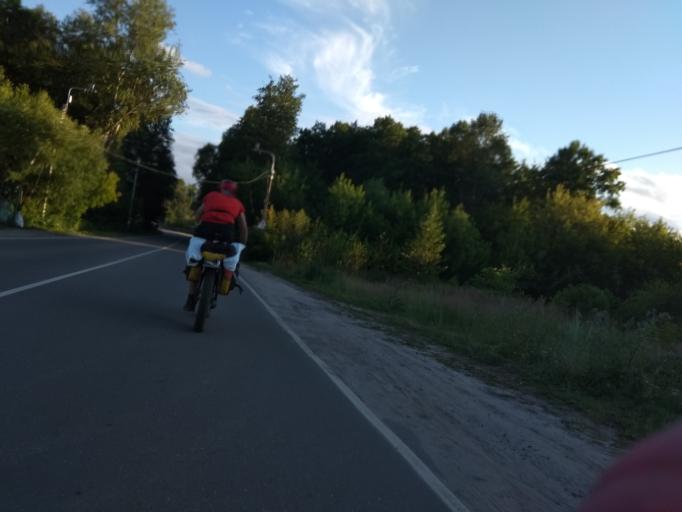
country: RU
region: Moskovskaya
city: Misheronskiy
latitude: 55.7170
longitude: 39.7398
